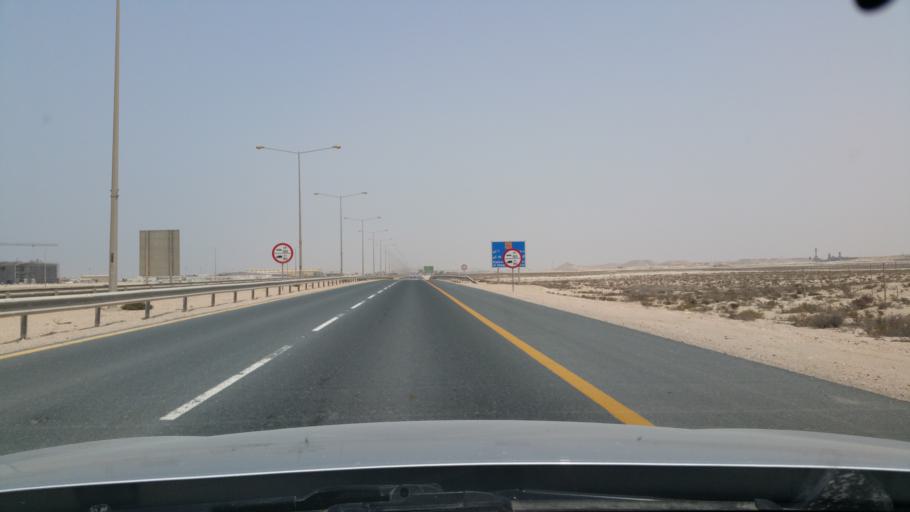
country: QA
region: Baladiyat ar Rayyan
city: Dukhan
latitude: 25.3696
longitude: 50.7805
